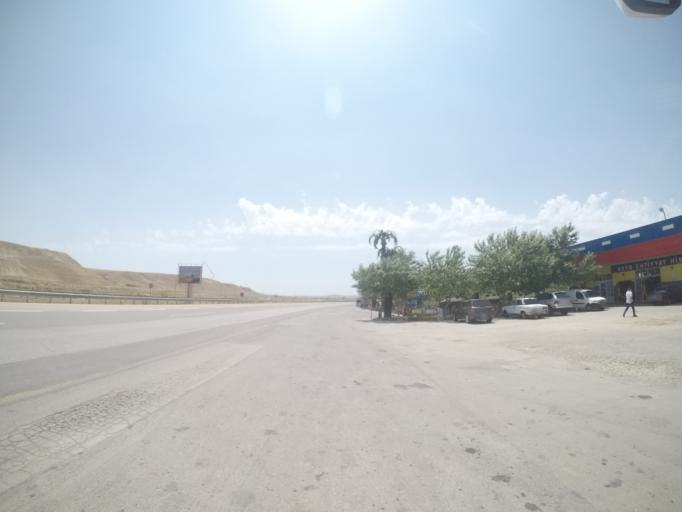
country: AZ
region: Haciqabul
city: Haciqabul
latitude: 40.0202
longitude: 48.9546
